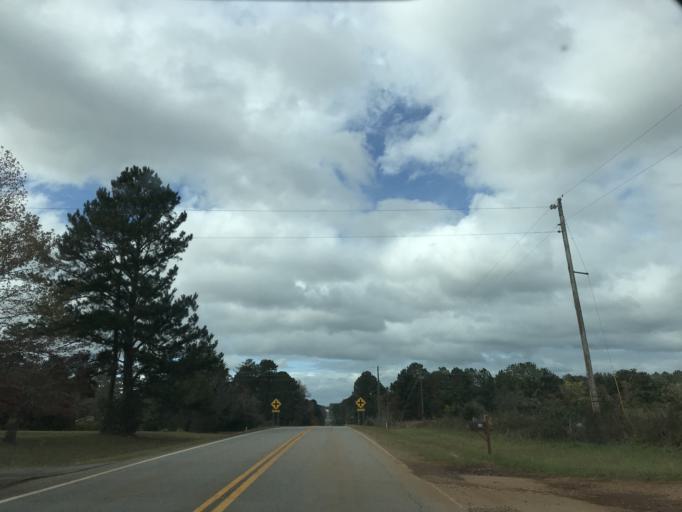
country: US
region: Georgia
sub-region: Jones County
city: Gray
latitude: 32.9794
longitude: -83.5071
